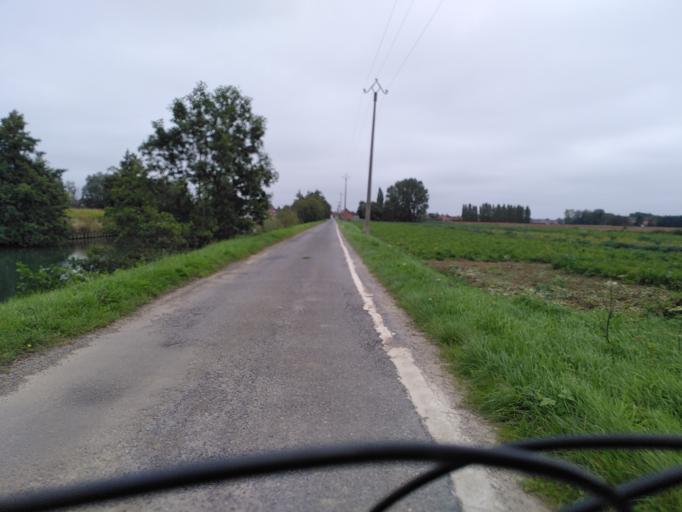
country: FR
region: Nord-Pas-de-Calais
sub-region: Departement du Pas-de-Calais
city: Calonne-sur-la-Lys
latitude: 50.6355
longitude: 2.6154
